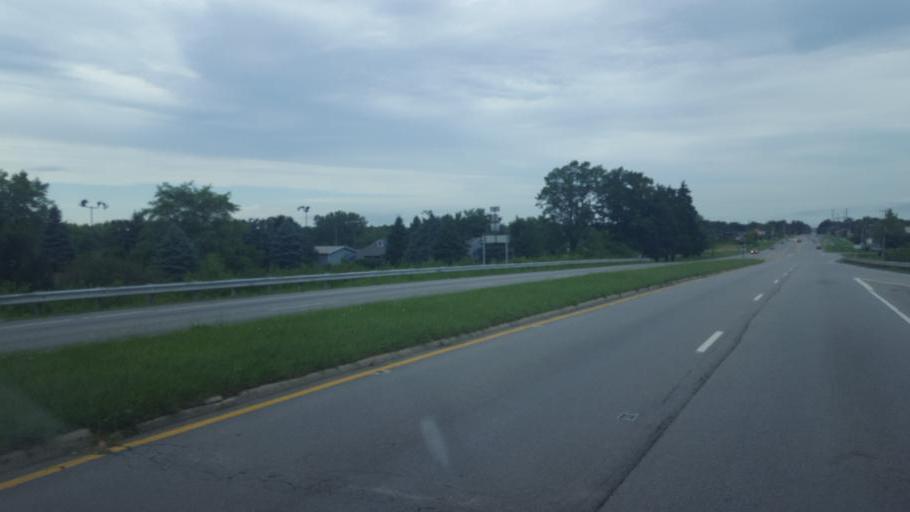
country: US
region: Ohio
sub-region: Franklin County
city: Groveport
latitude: 39.8909
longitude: -82.8828
